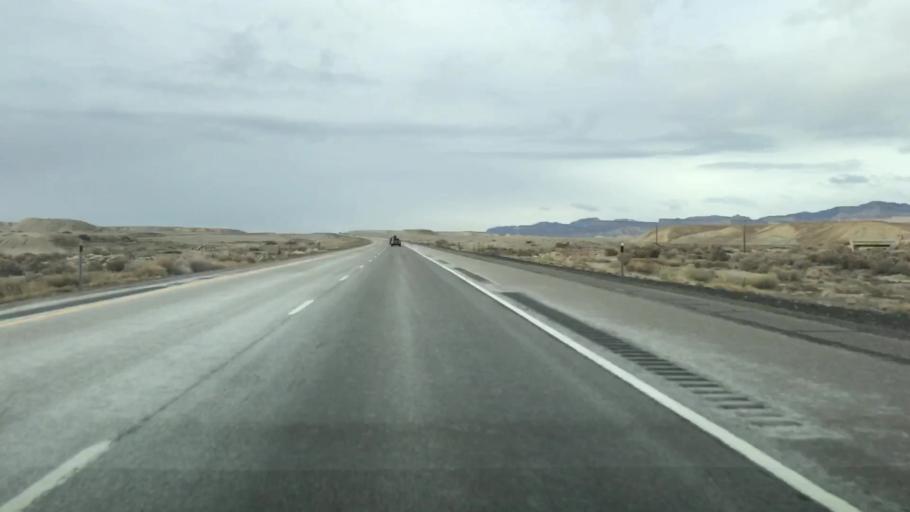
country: US
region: Utah
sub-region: Grand County
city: Moab
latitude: 38.9421
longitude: -109.5225
